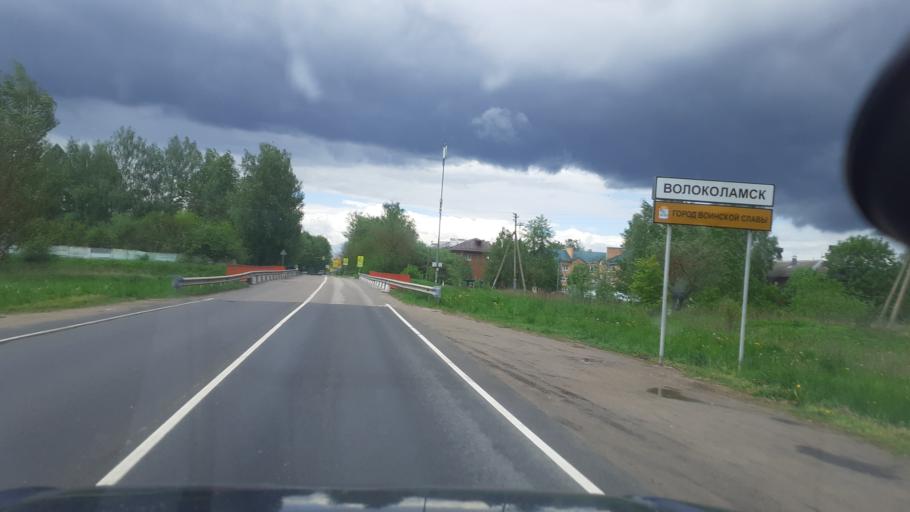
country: RU
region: Moskovskaya
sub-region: Volokolamskiy Rayon
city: Volokolamsk
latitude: 56.0249
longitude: 35.9648
